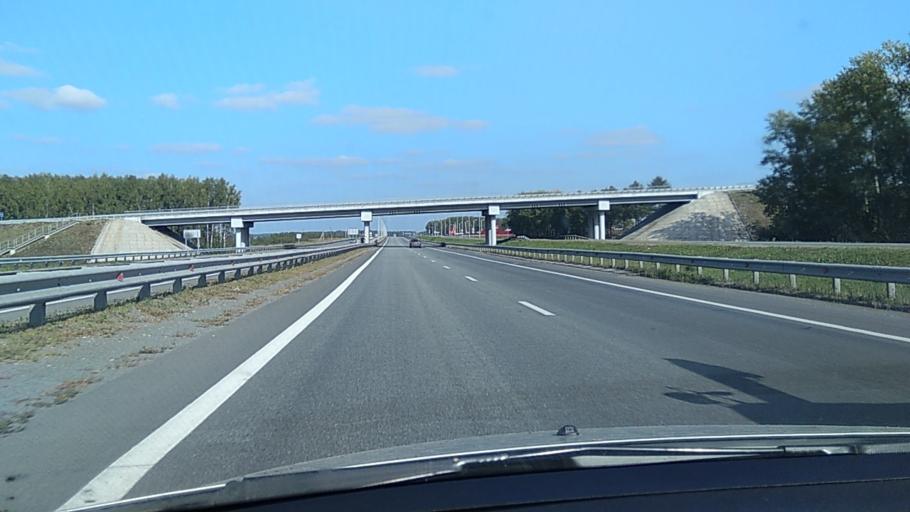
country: RU
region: Chelyabinsk
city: Timiryazevskiy
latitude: 54.9306
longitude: 60.7433
